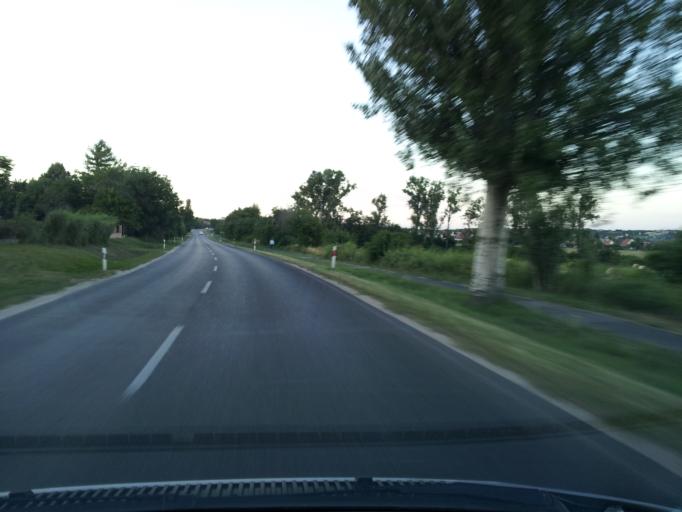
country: HU
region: Veszprem
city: Balatonalmadi
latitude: 47.0544
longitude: 18.0206
